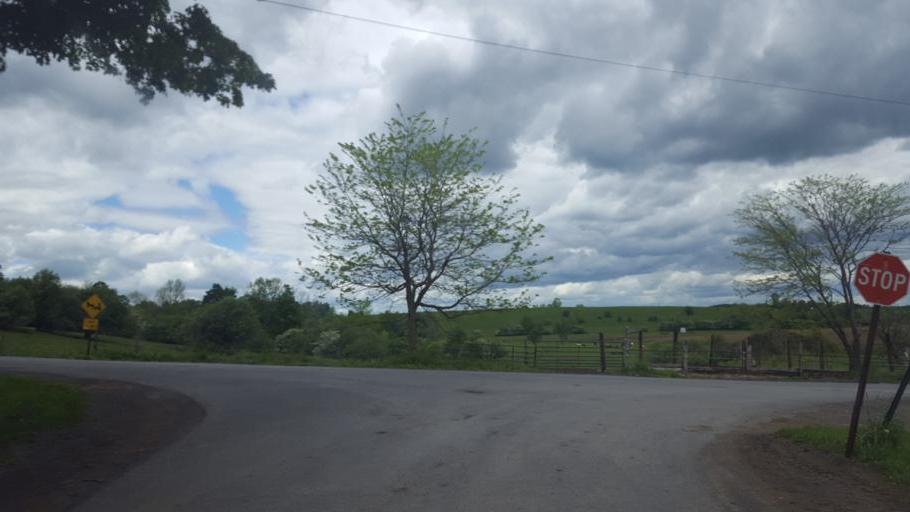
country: US
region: New York
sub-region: Otsego County
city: Richfield Springs
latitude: 42.8759
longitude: -75.0257
